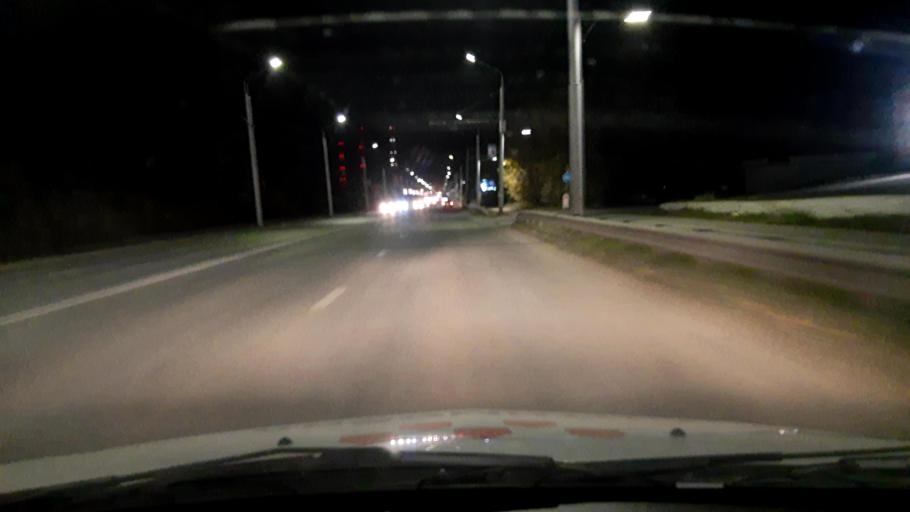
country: RU
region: Bashkortostan
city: Ufa
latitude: 54.7911
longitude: 56.0909
